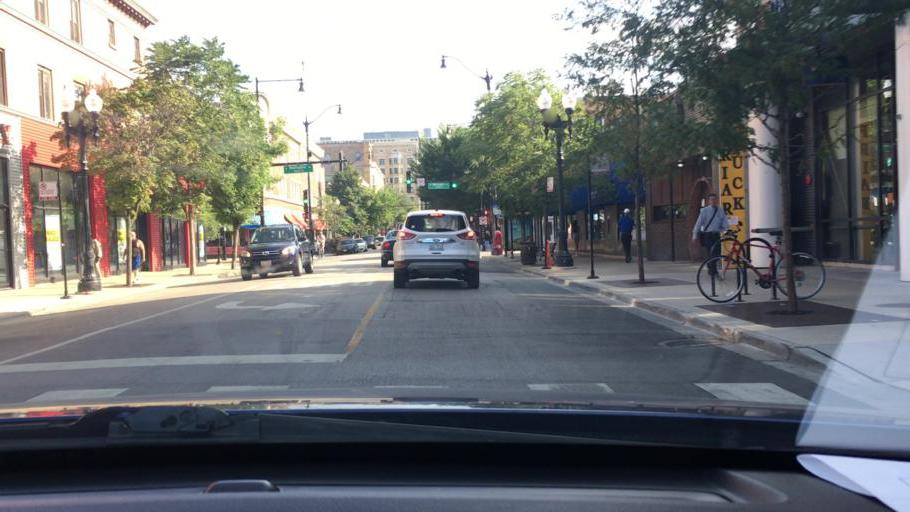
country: US
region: Illinois
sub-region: Cook County
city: Chicago
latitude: 41.9364
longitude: -87.6443
